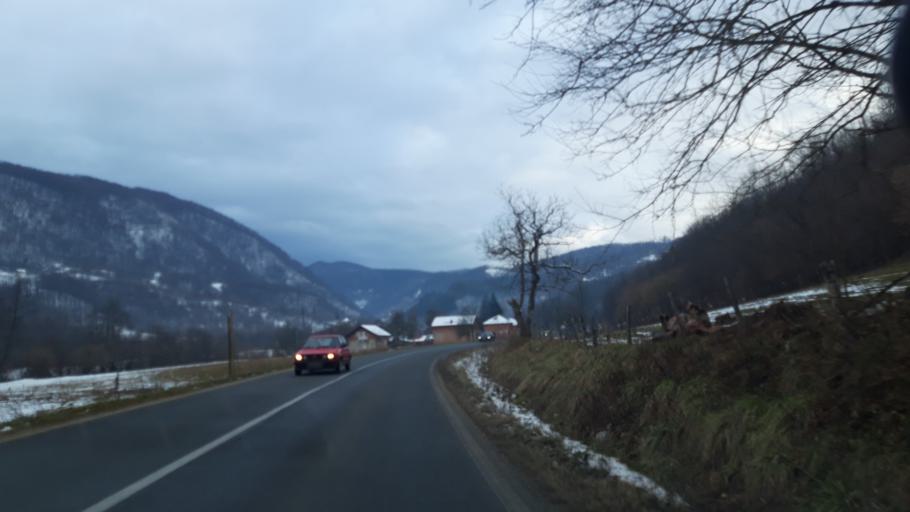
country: BA
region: Republika Srpska
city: Milici
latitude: 44.1695
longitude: 19.0226
